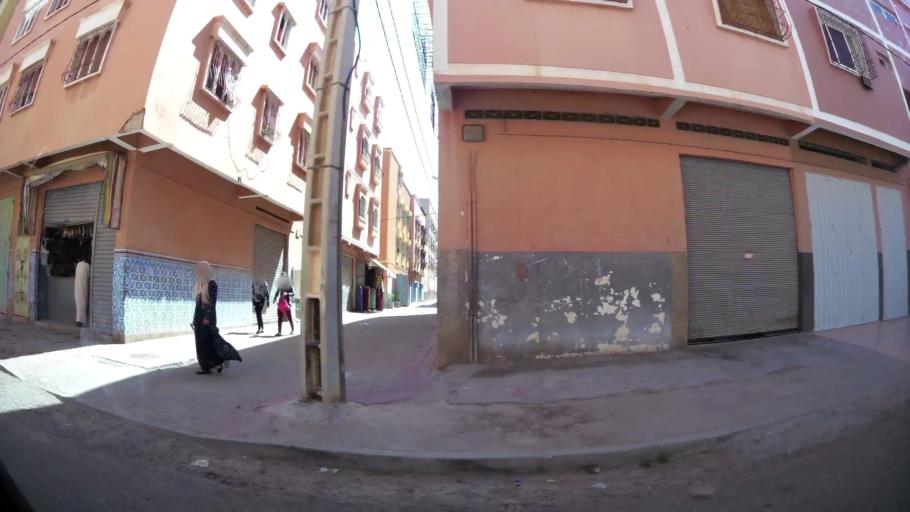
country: MA
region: Souss-Massa-Draa
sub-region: Inezgane-Ait Mellou
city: Inezgane
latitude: 30.3349
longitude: -9.5053
